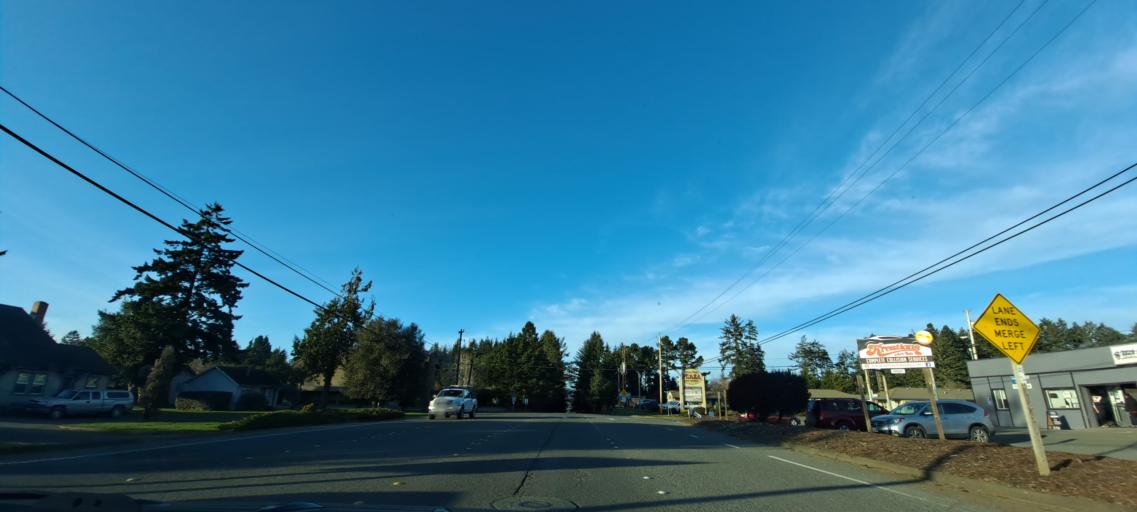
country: US
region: California
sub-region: Humboldt County
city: McKinleyville
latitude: 40.9263
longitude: -124.1008
